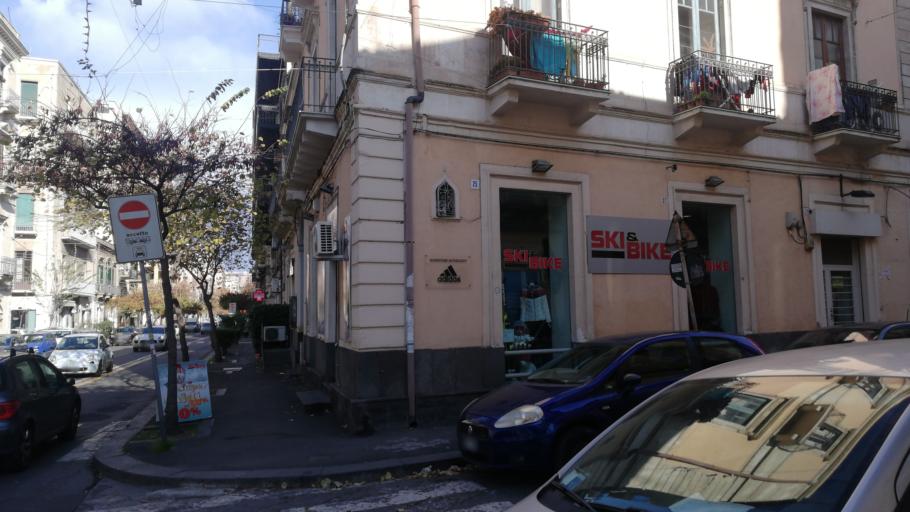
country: IT
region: Sicily
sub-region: Catania
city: Canalicchio
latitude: 37.5136
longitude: 15.0976
